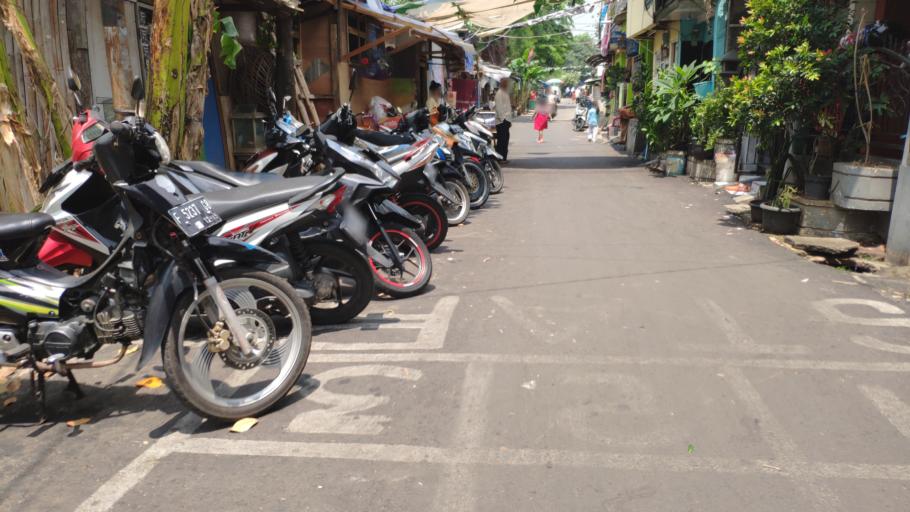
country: ID
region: Jakarta Raya
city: Jakarta
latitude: -6.2071
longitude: 106.8605
